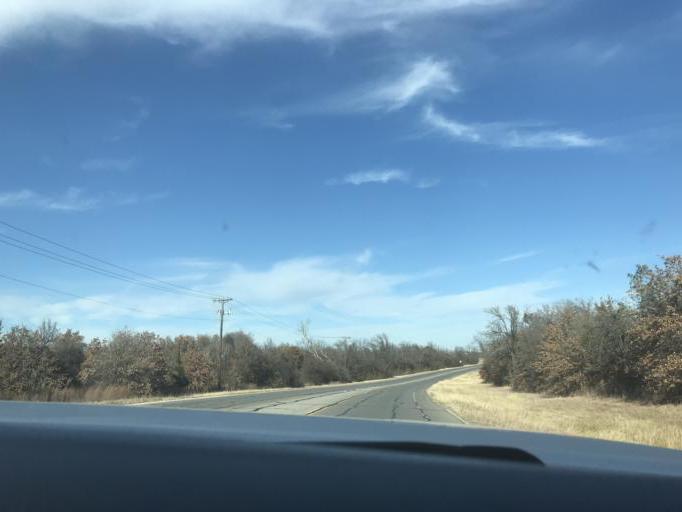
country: US
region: Texas
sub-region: Erath County
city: Stephenville
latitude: 32.2106
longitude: -98.2469
